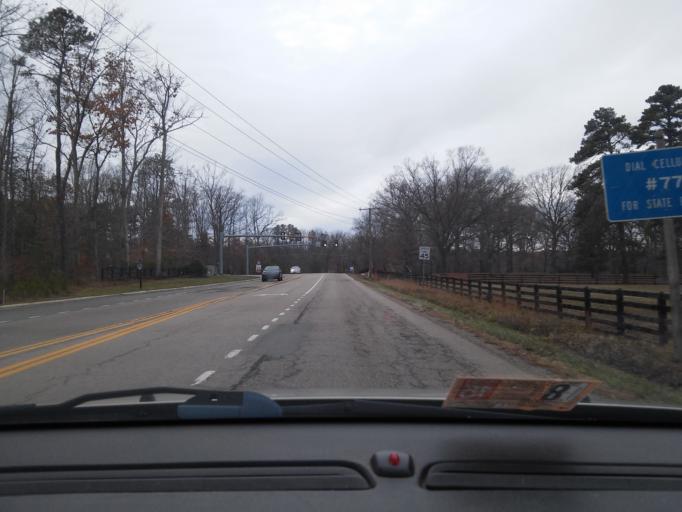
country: US
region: Virginia
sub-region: Henrico County
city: Short Pump
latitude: 37.5546
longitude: -77.6679
